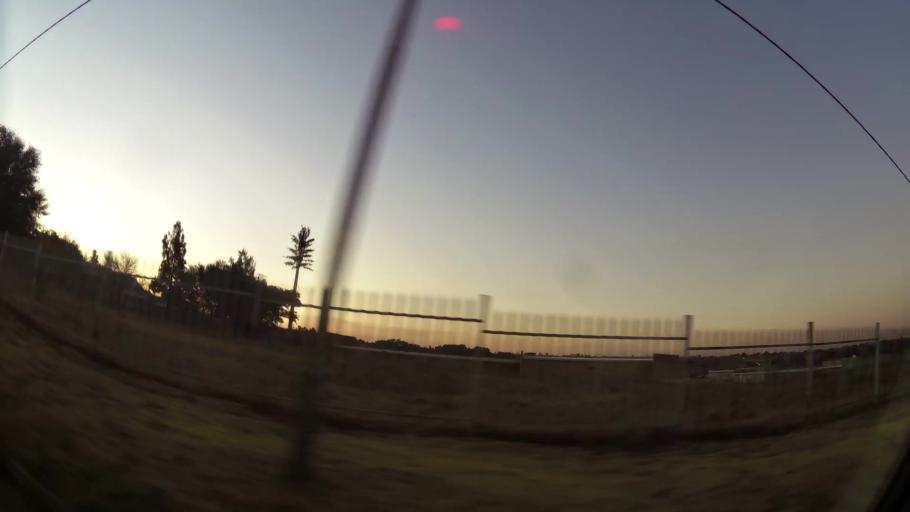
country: ZA
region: Gauteng
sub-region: Ekurhuleni Metropolitan Municipality
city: Germiston
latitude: -26.2575
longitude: 28.1593
